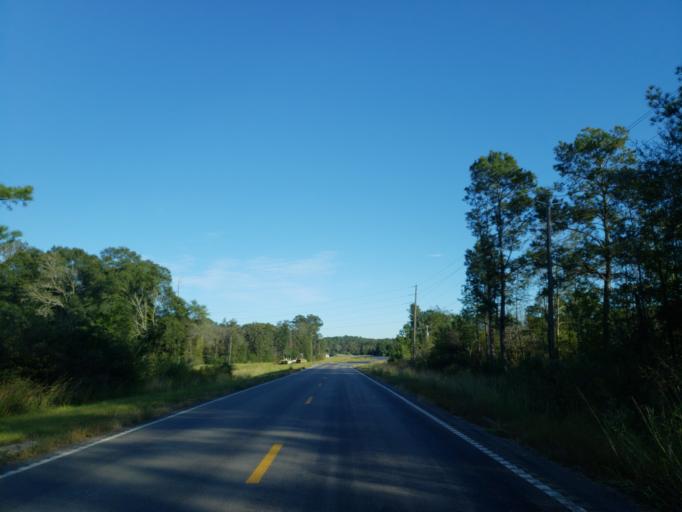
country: US
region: Mississippi
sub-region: Perry County
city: Richton
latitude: 31.3681
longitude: -88.8167
